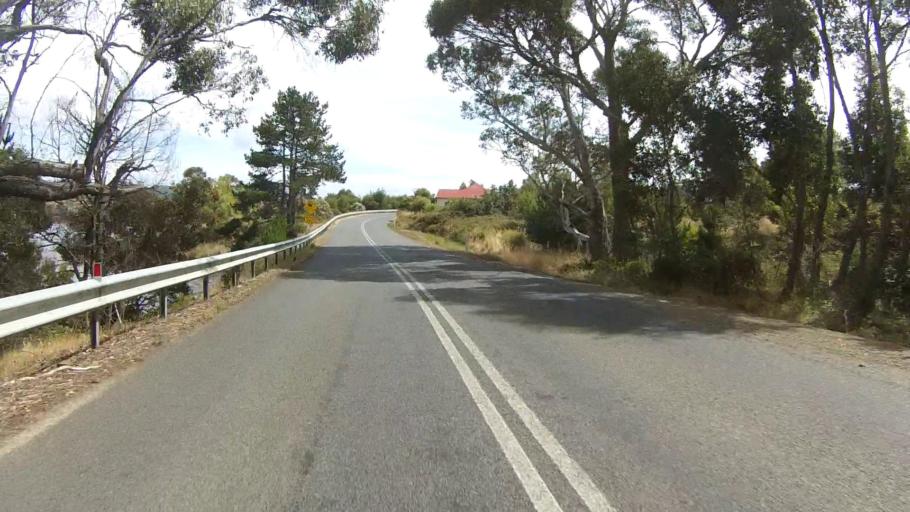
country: AU
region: Tasmania
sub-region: Huon Valley
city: Cygnet
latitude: -43.1905
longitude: 147.1014
